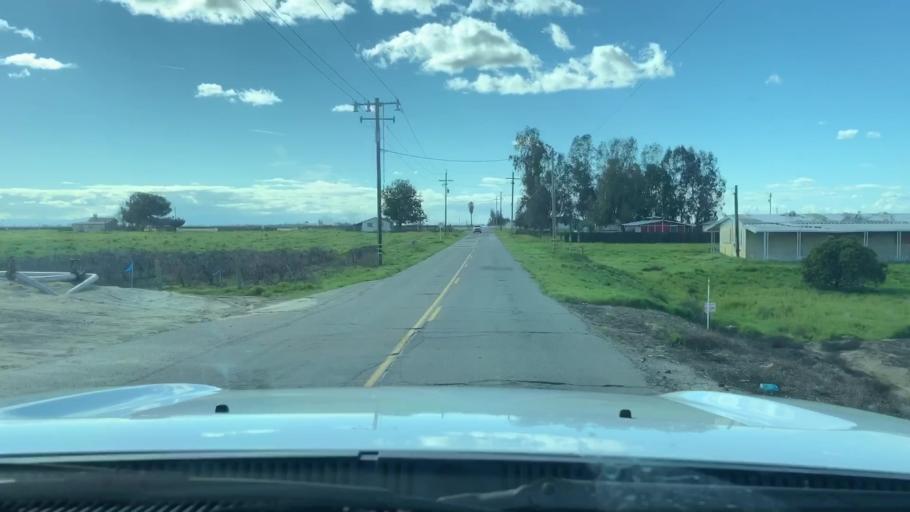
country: US
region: California
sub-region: Fresno County
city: Fowler
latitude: 36.5619
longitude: -119.7413
